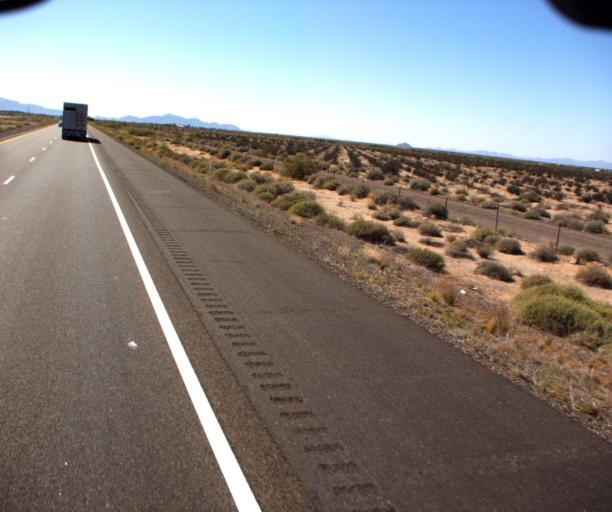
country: US
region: Arizona
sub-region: Yuma County
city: Wellton
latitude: 32.8159
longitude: -113.5010
